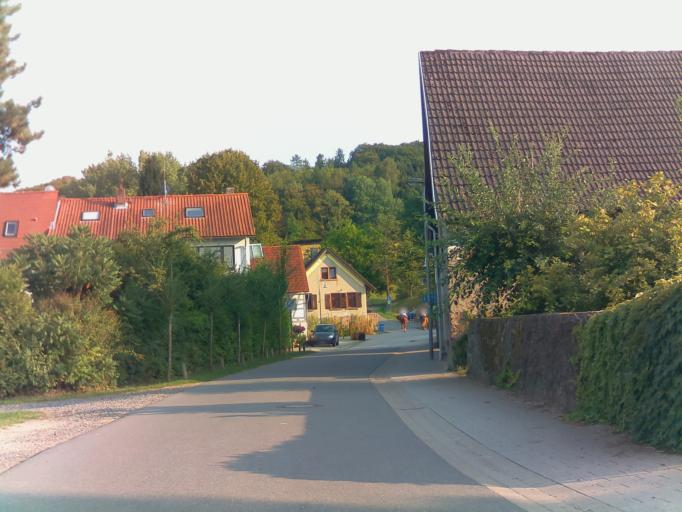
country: DE
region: Hesse
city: Lutzelbach
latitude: 49.7614
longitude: 8.7381
